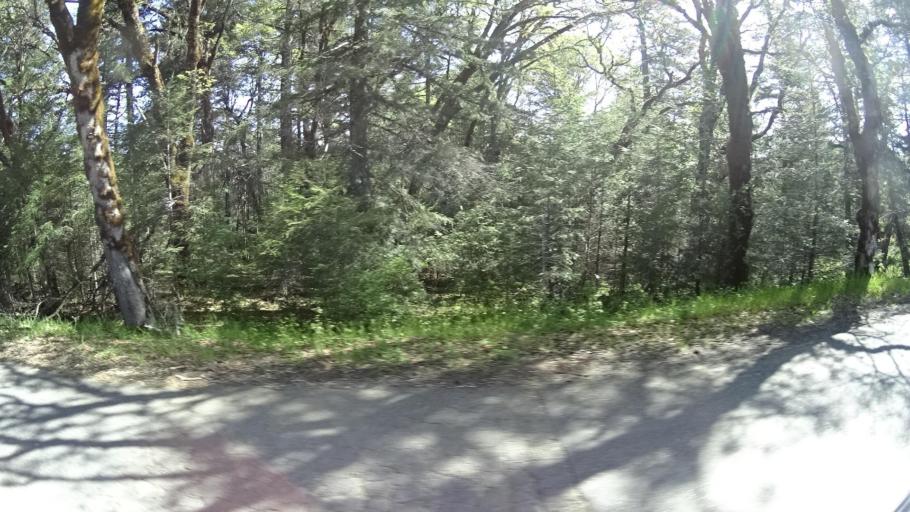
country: US
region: California
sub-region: Humboldt County
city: Redway
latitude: 40.0631
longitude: -123.6432
